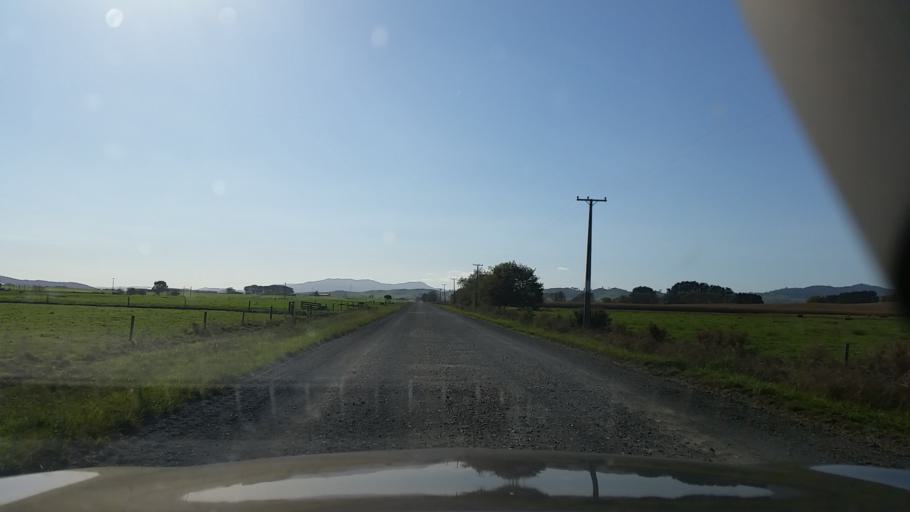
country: NZ
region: Waikato
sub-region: Hamilton City
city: Hamilton
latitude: -37.6365
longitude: 175.4300
